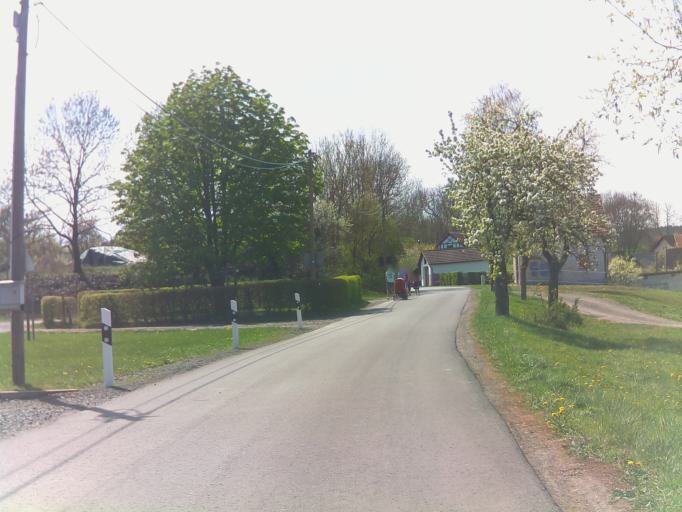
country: DE
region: Bavaria
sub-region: Regierungsbezirk Unterfranken
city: Ermershausen
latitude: 50.2391
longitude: 10.6342
